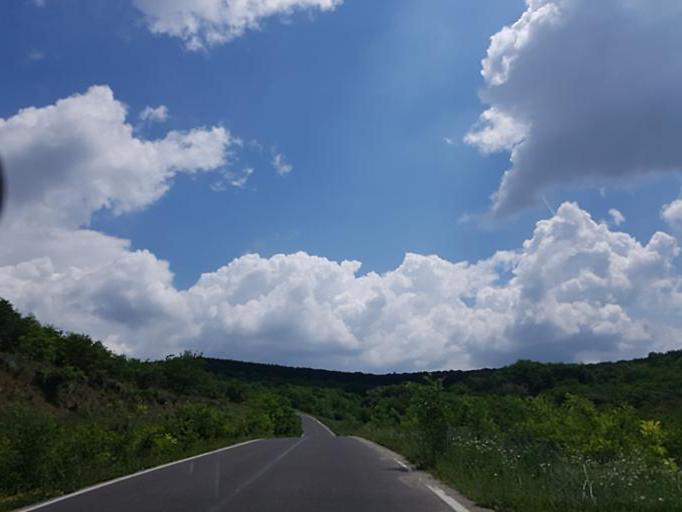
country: RO
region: Sibiu
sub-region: Comuna Seica Mica
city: Seica Mica
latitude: 46.0482
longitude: 24.1508
